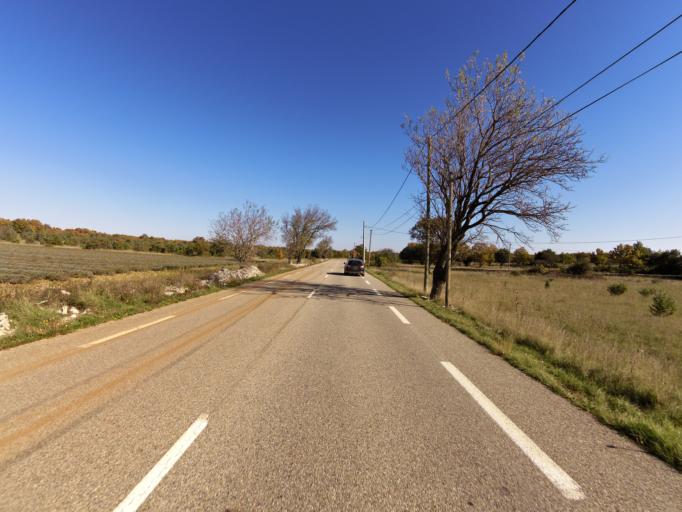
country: FR
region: Rhone-Alpes
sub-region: Departement de l'Ardeche
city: Bourg-Saint-Andeol
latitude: 44.3928
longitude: 4.5432
